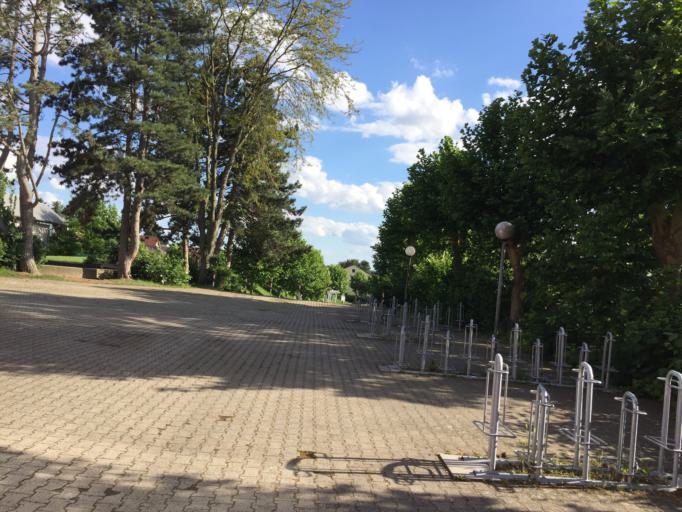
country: DE
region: Hesse
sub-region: Regierungsbezirk Darmstadt
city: Karben
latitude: 50.2354
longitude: 8.7750
